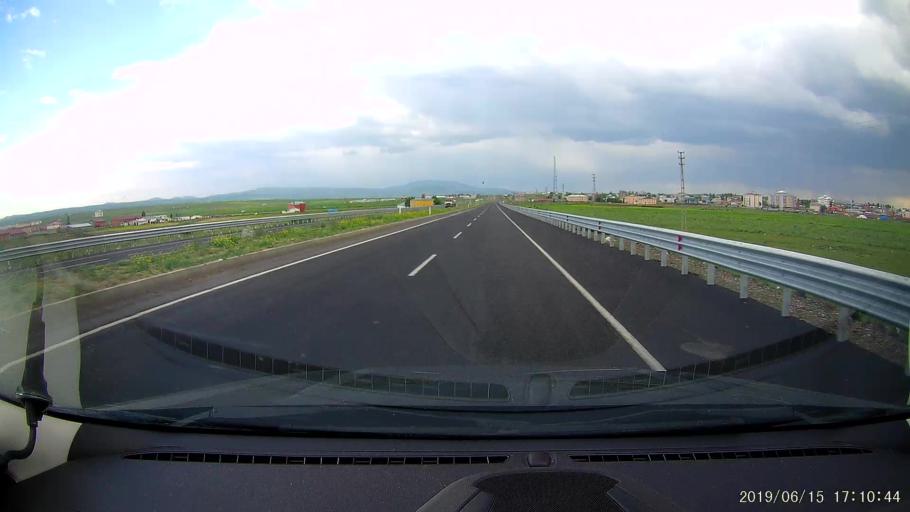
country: TR
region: Kars
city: Kars
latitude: 40.6190
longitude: 43.1335
